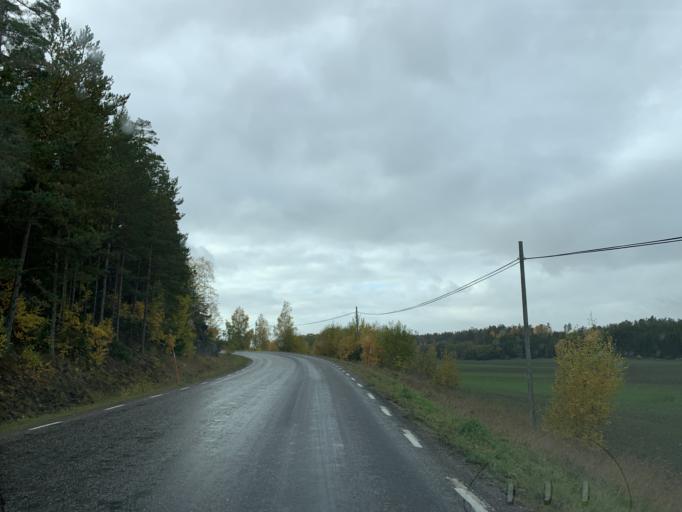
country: SE
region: Stockholm
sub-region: Nynashamns Kommun
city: Osmo
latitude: 58.9487
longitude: 17.7637
